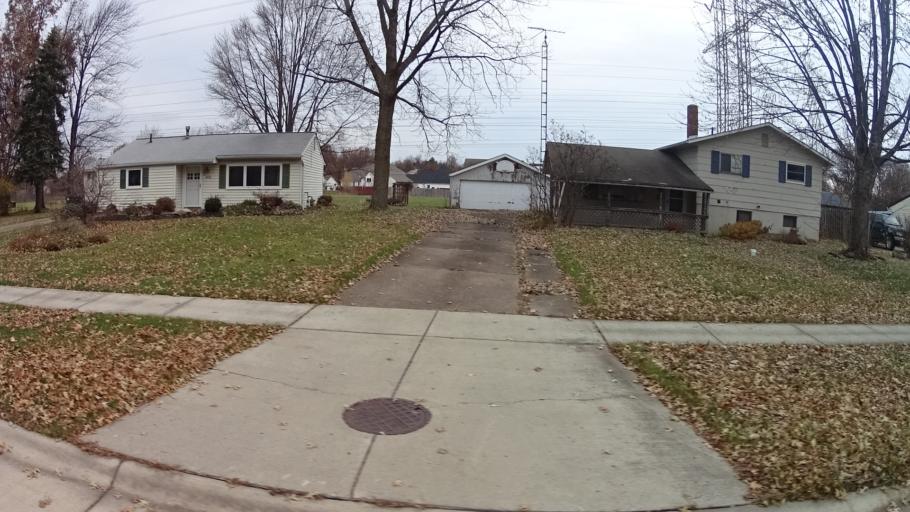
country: US
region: Ohio
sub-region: Lorain County
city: North Ridgeville
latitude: 41.4074
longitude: -82.0050
